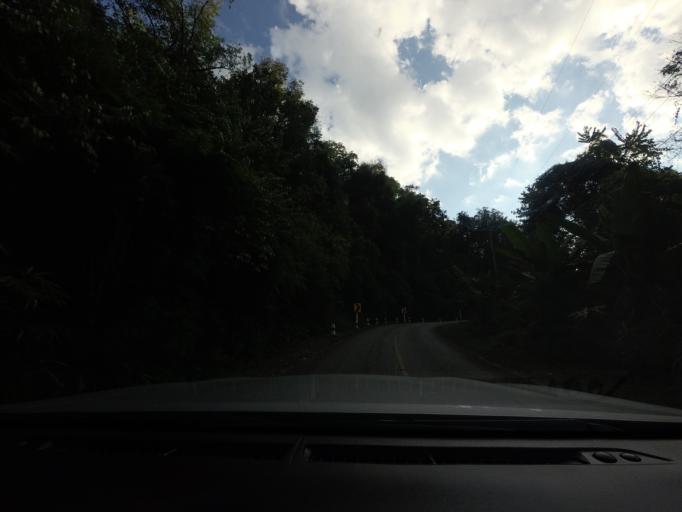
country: TH
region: Chiang Mai
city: Phrao
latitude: 19.5084
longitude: 99.1721
